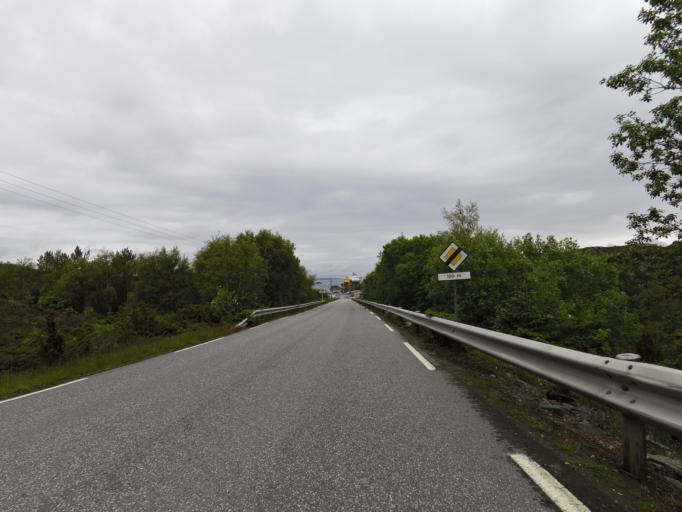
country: NO
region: Hordaland
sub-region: Sveio
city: Sveio
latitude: 59.6056
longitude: 5.2328
